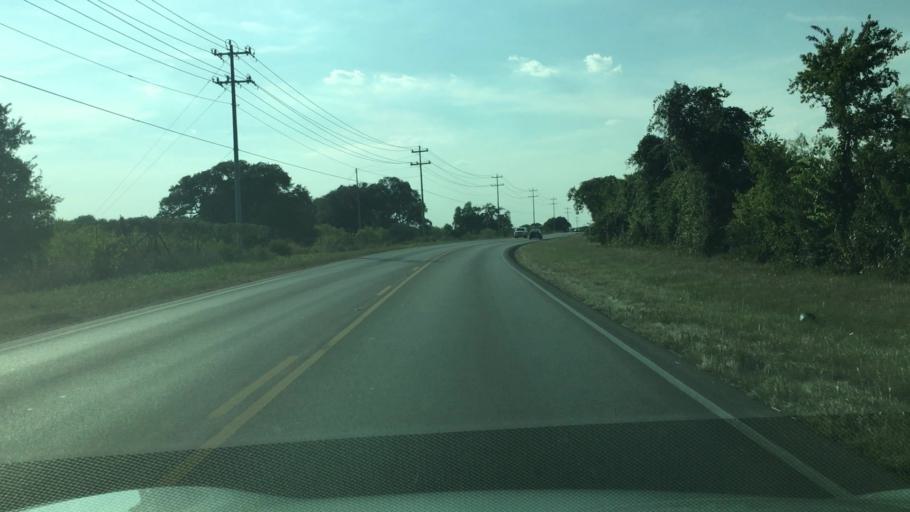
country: US
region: Texas
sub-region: Hays County
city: Buda
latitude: 30.1006
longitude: -97.9367
